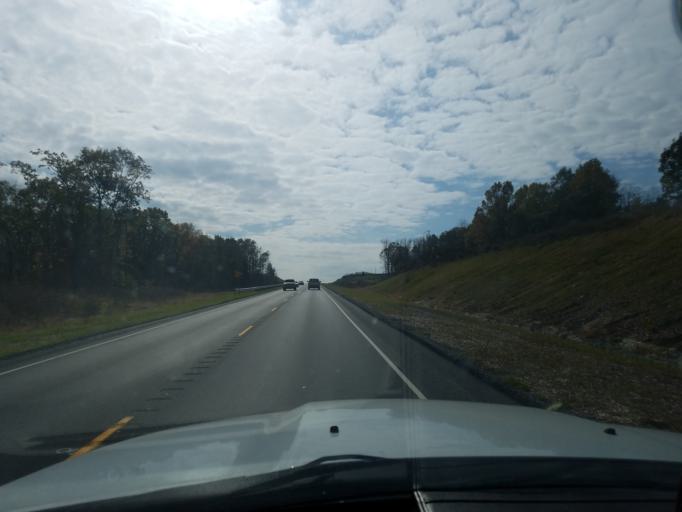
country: US
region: Kentucky
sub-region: Bullitt County
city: Mount Washington
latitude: 37.9839
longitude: -85.4916
